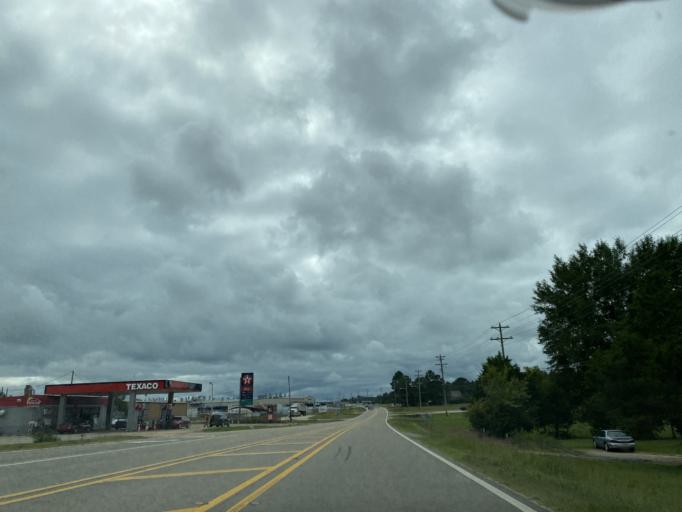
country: US
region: Mississippi
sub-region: Tishomingo County
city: Belmont
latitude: 34.4883
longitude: -88.2070
